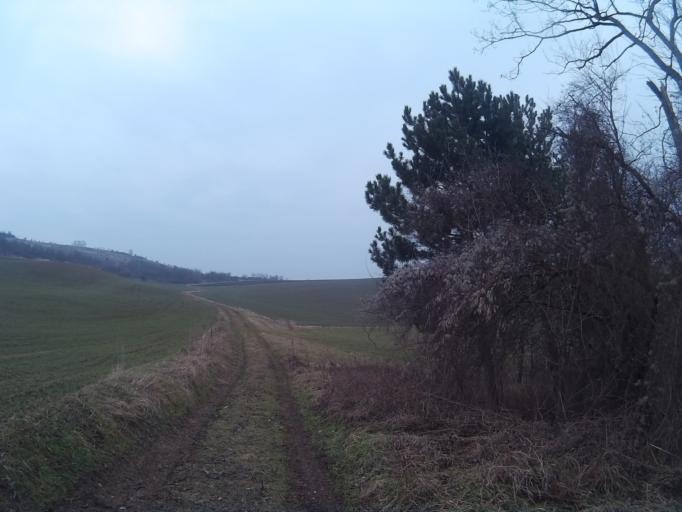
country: HU
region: Fejer
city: Many
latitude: 47.5388
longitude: 18.6002
